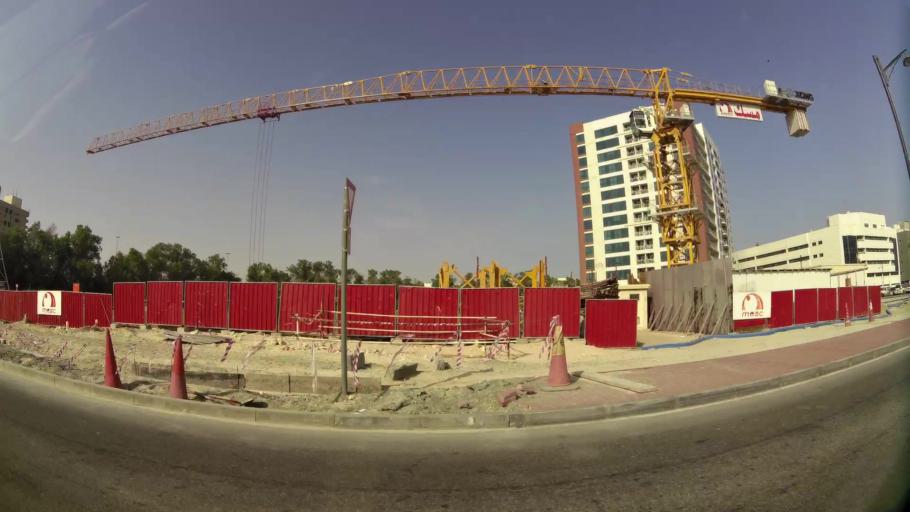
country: AE
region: Ash Shariqah
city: Sharjah
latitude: 25.2830
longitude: 55.3563
